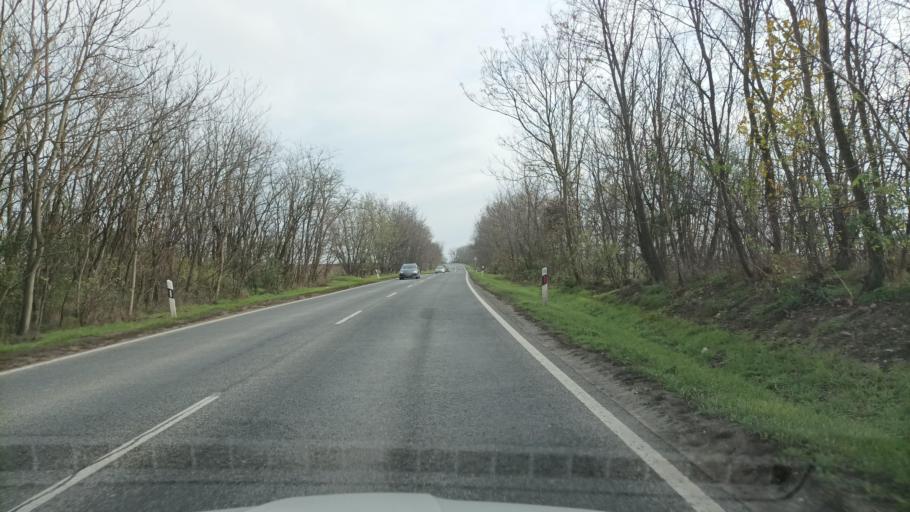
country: HU
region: Pest
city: Alsonemedi
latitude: 47.3259
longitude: 19.1902
